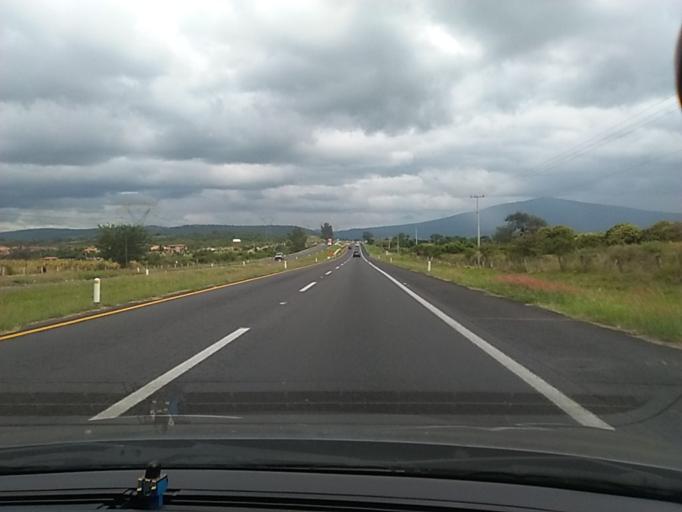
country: MX
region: Jalisco
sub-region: Zapotlanejo
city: La Mezquitera
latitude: 20.5962
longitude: -103.1122
